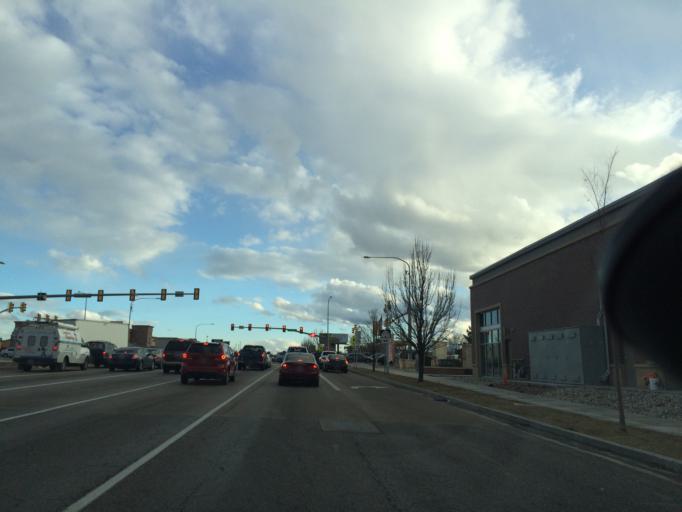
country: US
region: Utah
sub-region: Salt Lake County
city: Taylorsville
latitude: 40.6541
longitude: -111.9390
